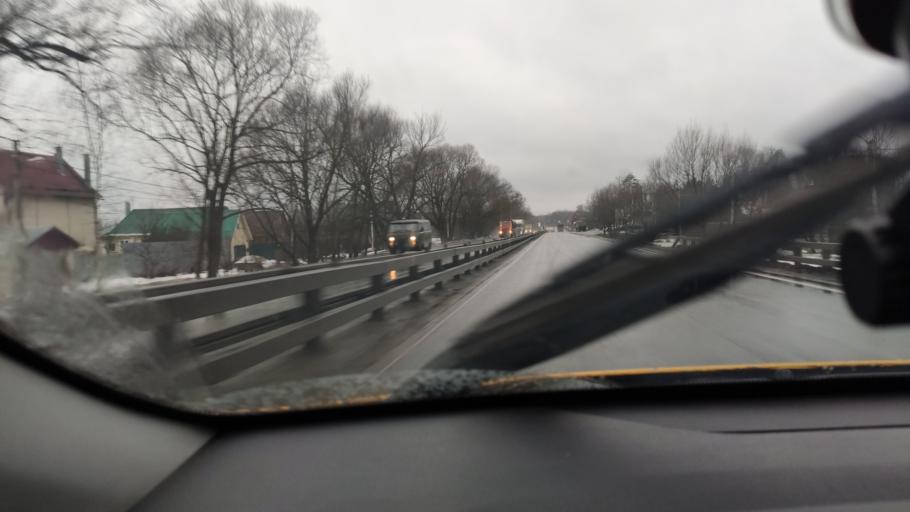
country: RU
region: Moskovskaya
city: Troitsk
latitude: 55.3032
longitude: 37.2165
